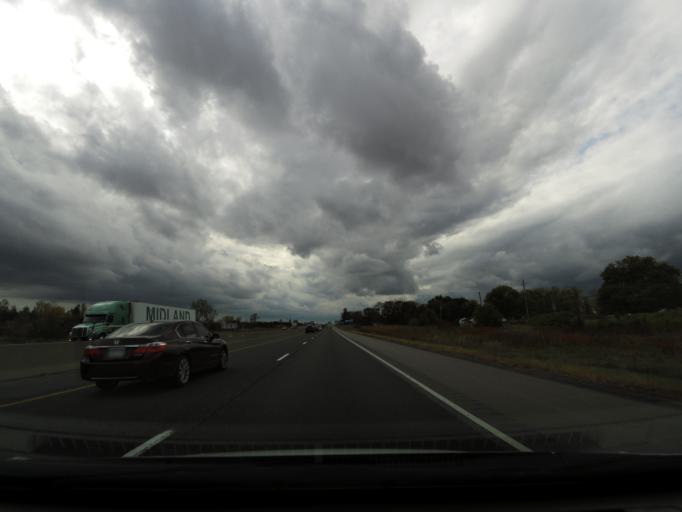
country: CA
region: Ontario
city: Belleville
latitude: 44.1856
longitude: -77.4237
